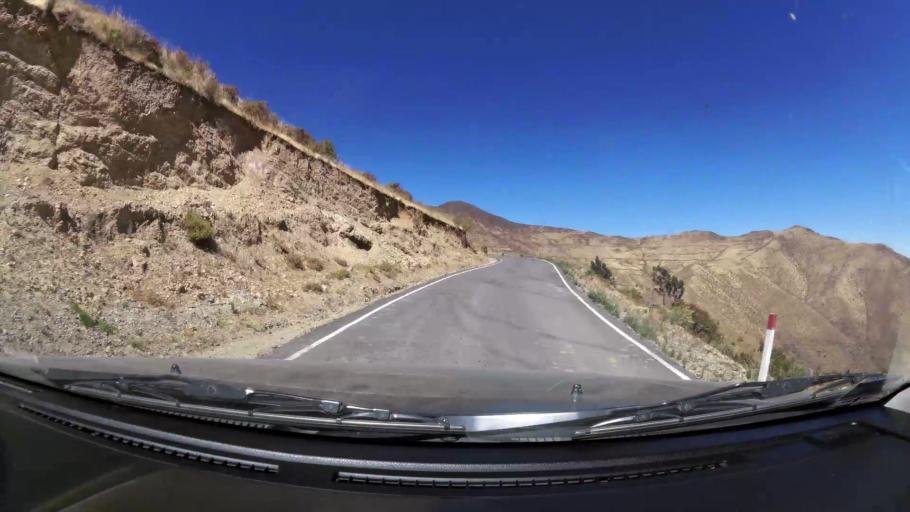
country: PE
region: Huancavelica
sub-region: Huaytara
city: Quito-Arma
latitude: -13.6843
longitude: -75.3842
